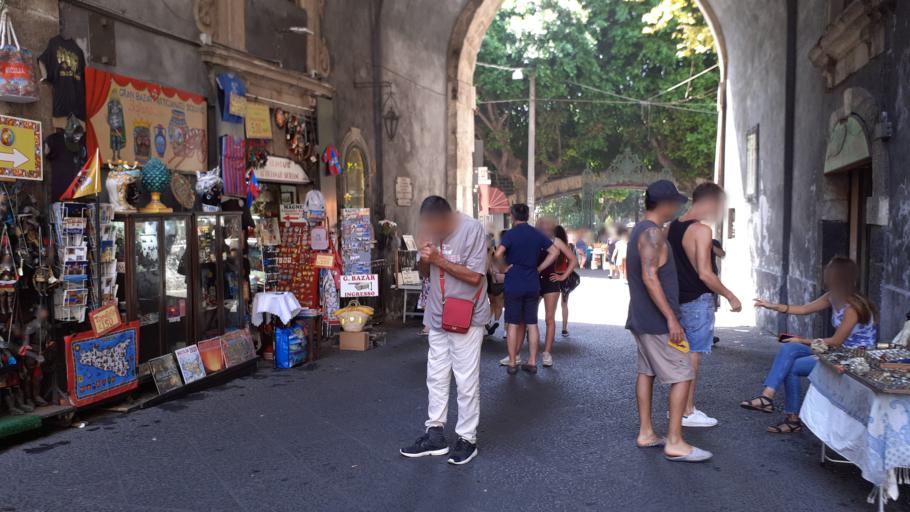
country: IT
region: Sicily
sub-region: Catania
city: Catania
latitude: 37.5019
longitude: 15.0876
